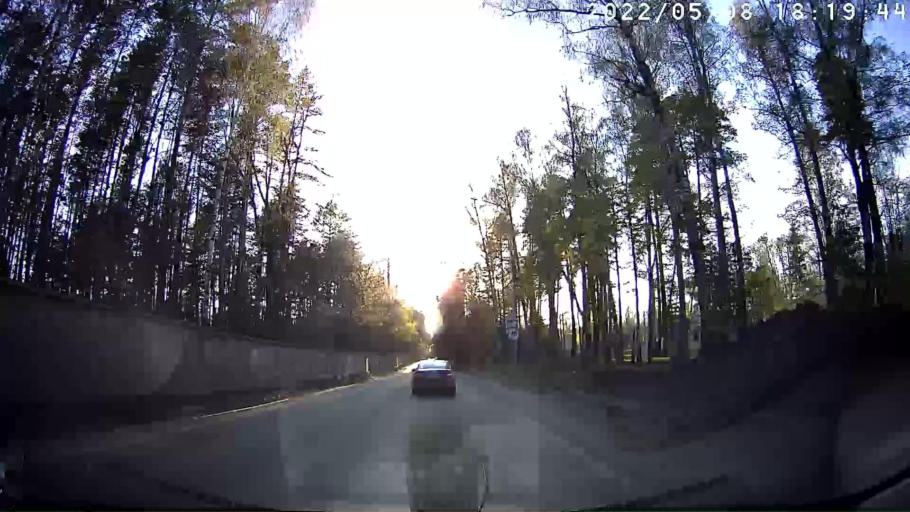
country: RU
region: Tatarstan
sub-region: Zelenodol'skiy Rayon
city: Zelenodolsk
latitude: 55.8396
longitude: 48.4403
